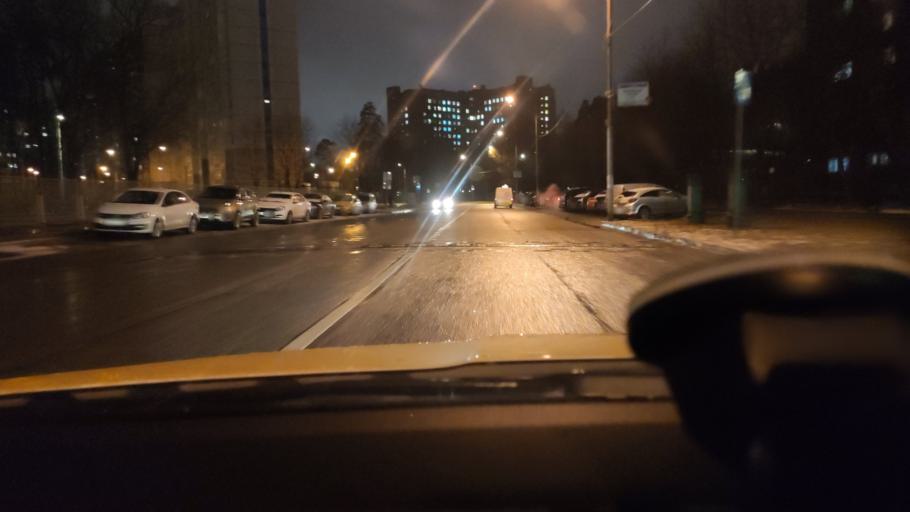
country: RU
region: Moscow
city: Yaroslavskiy
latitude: 55.8859
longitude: 37.7078
